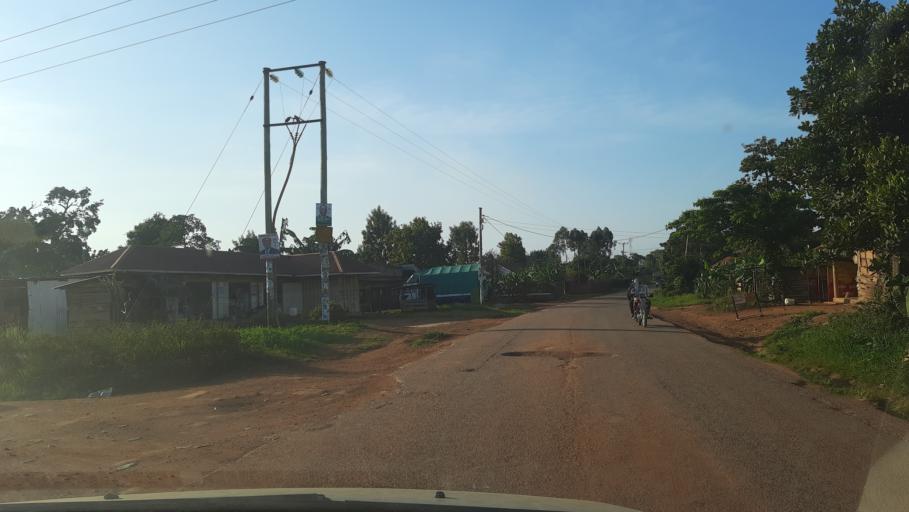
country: UG
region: Central Region
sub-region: Mukono District
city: Mukono
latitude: 0.3765
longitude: 32.7465
